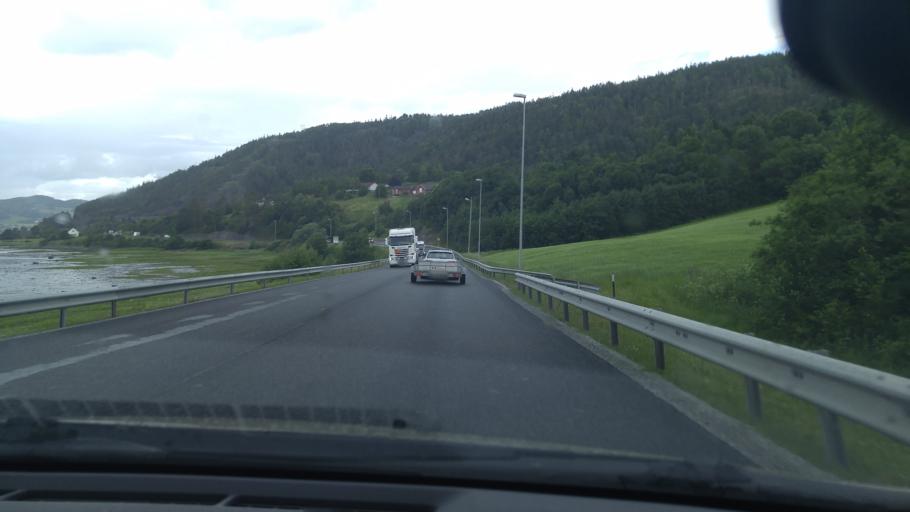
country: NO
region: Nord-Trondelag
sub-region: Verdal
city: Verdal
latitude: 63.8306
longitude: 11.4416
